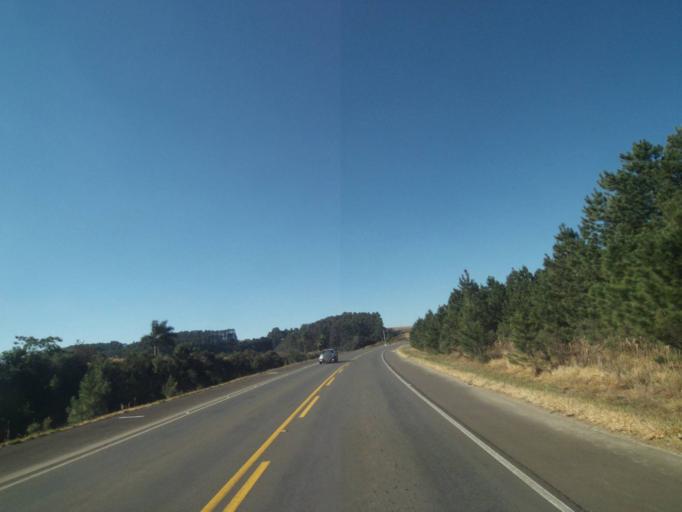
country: BR
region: Parana
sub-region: Tibagi
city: Tibagi
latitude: -24.8088
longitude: -50.4793
